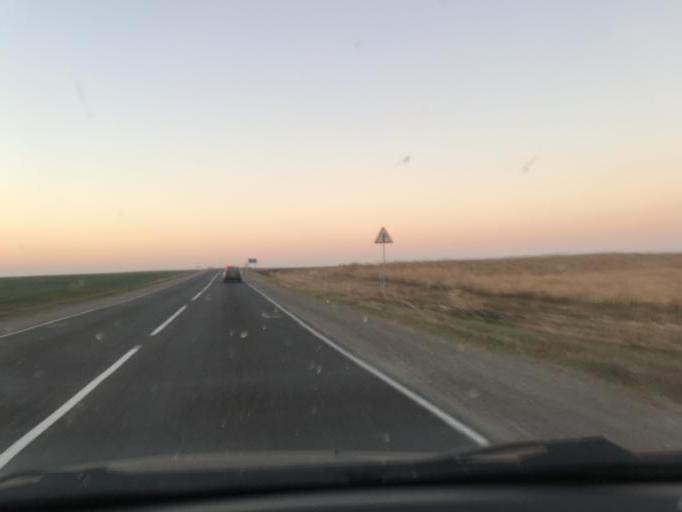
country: BY
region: Gomel
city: Horad Rechytsa
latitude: 52.2819
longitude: 30.4718
